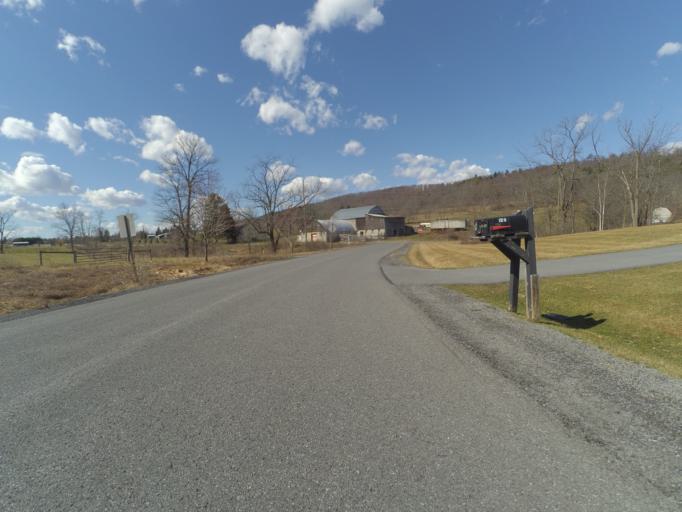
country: US
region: Pennsylvania
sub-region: Centre County
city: Park Forest Village
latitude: 40.8256
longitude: -77.9655
